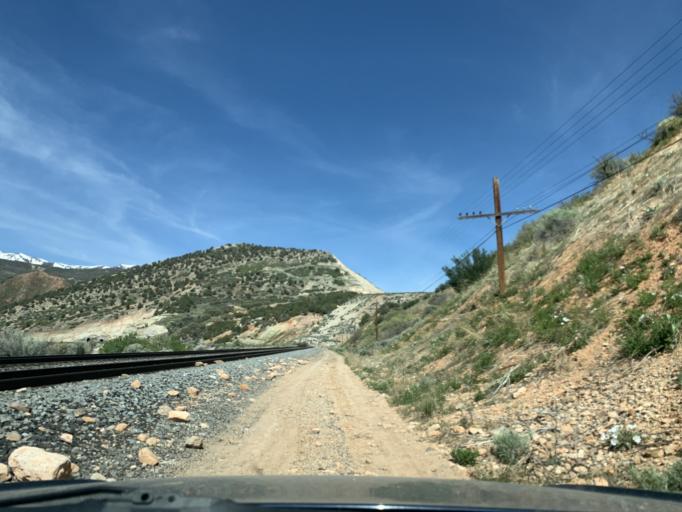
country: US
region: Utah
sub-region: Utah County
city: Mapleton
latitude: 39.9977
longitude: -111.4794
